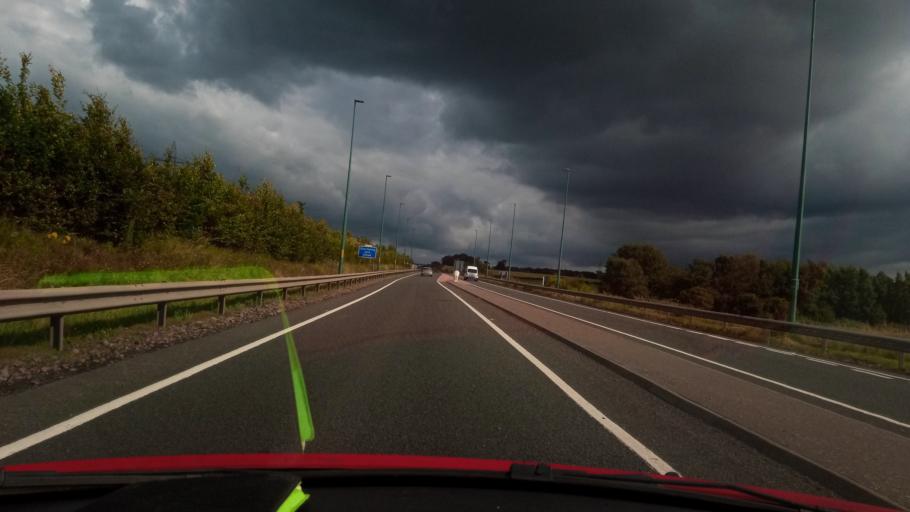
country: GB
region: Scotland
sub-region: Midlothian
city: Dalkeith
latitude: 55.9089
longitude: -3.0425
